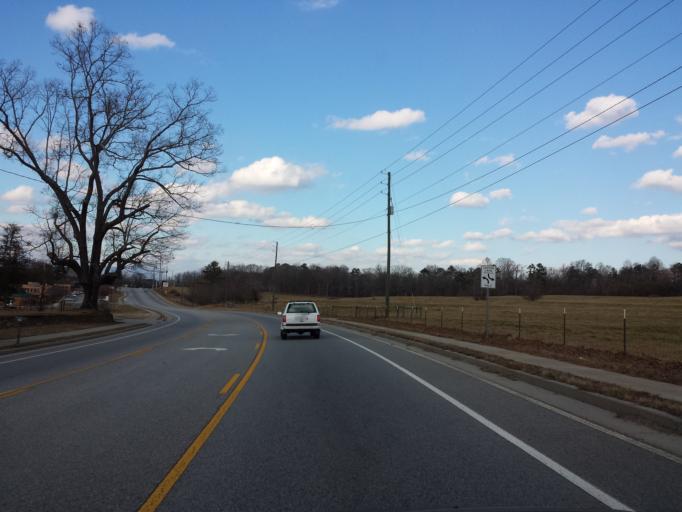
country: US
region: Georgia
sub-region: White County
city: Cleveland
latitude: 34.6141
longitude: -83.7543
